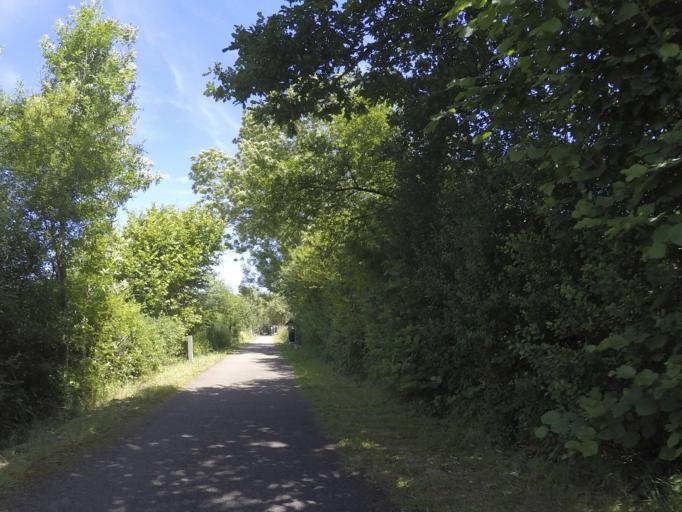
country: BE
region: Wallonia
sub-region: Province de Namur
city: Ciney
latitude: 50.3152
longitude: 5.1039
